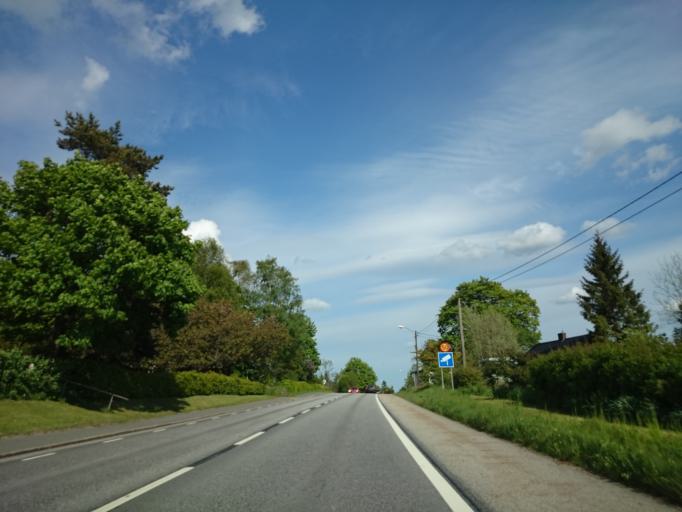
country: SE
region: Skane
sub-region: Horby Kommun
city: Hoerby
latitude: 55.9318
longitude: 13.8181
